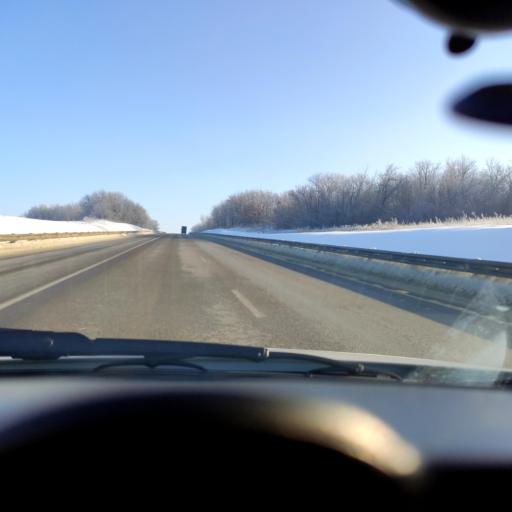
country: RU
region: Kursk
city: Tim
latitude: 51.6509
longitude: 37.0000
